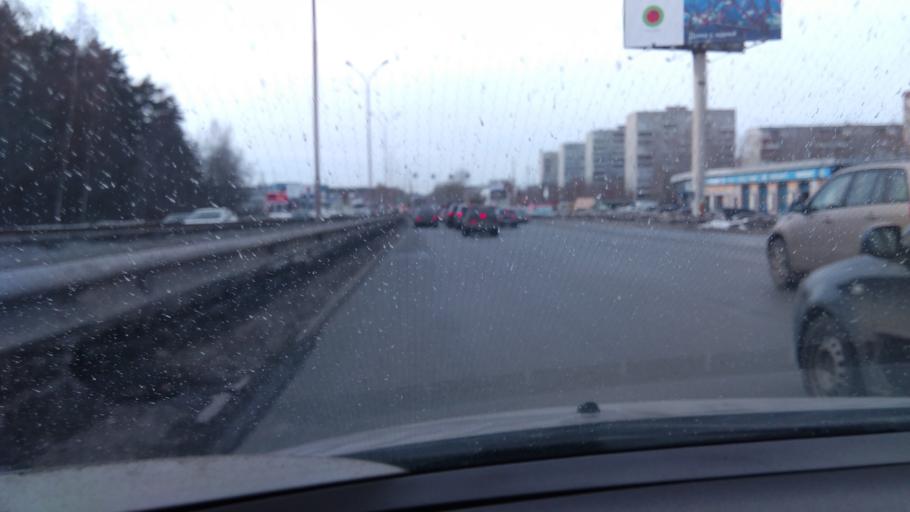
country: RU
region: Sverdlovsk
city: Sovkhoznyy
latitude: 56.7904
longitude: 60.5770
